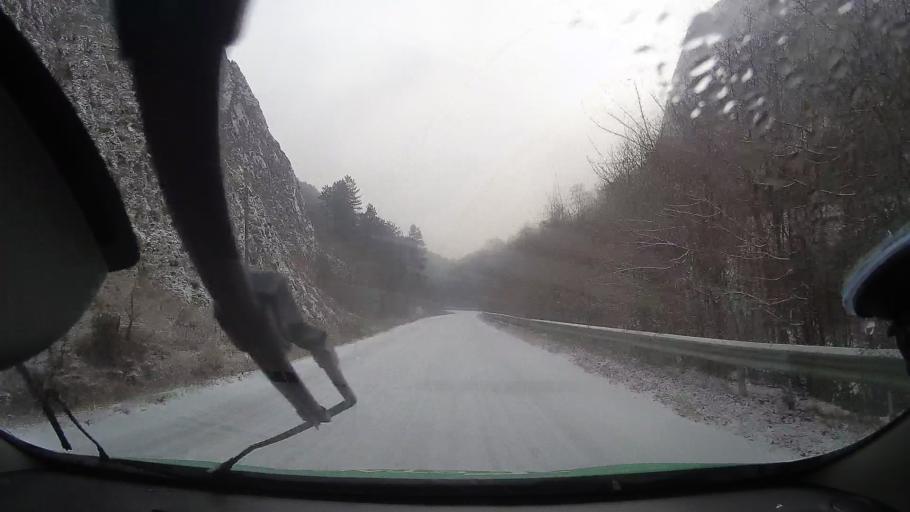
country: RO
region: Alba
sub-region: Comuna Livezile
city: Livezile
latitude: 46.3747
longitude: 23.5842
